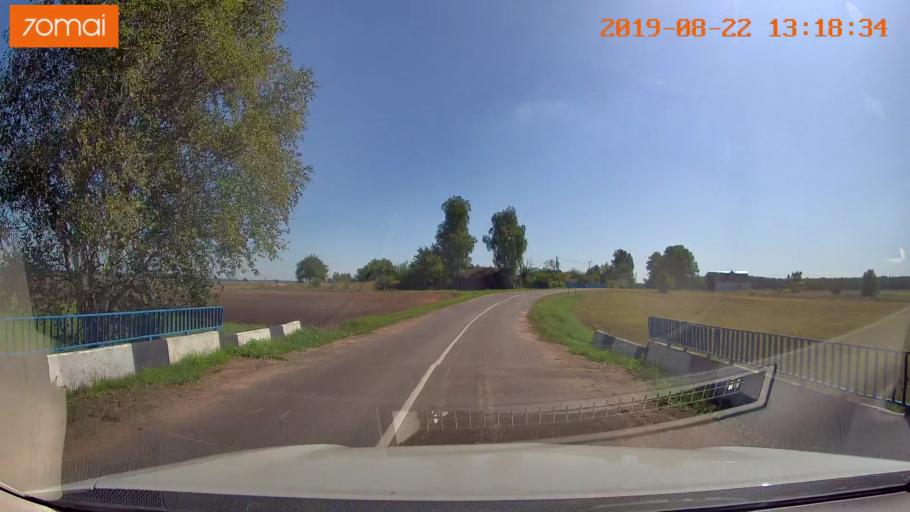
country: BY
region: Minsk
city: Urechcha
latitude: 53.2401
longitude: 27.9411
